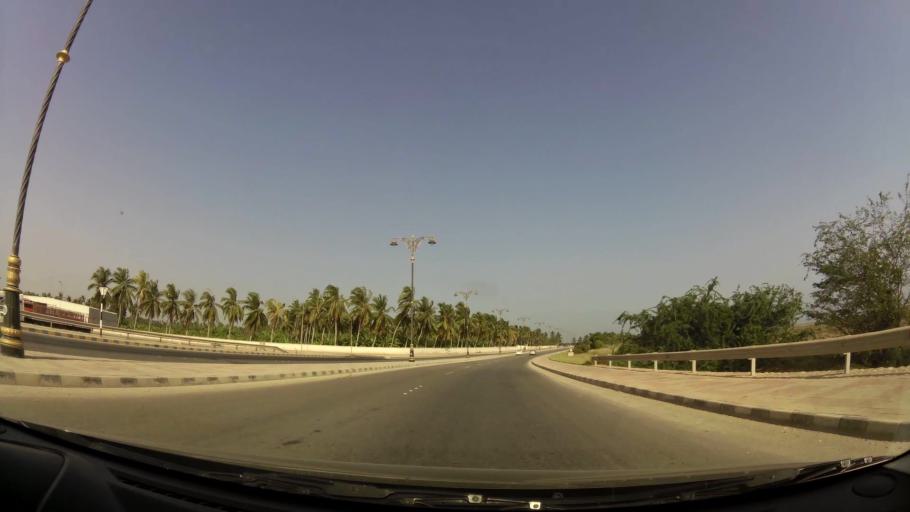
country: OM
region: Zufar
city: Salalah
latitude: 17.0018
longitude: 54.0678
